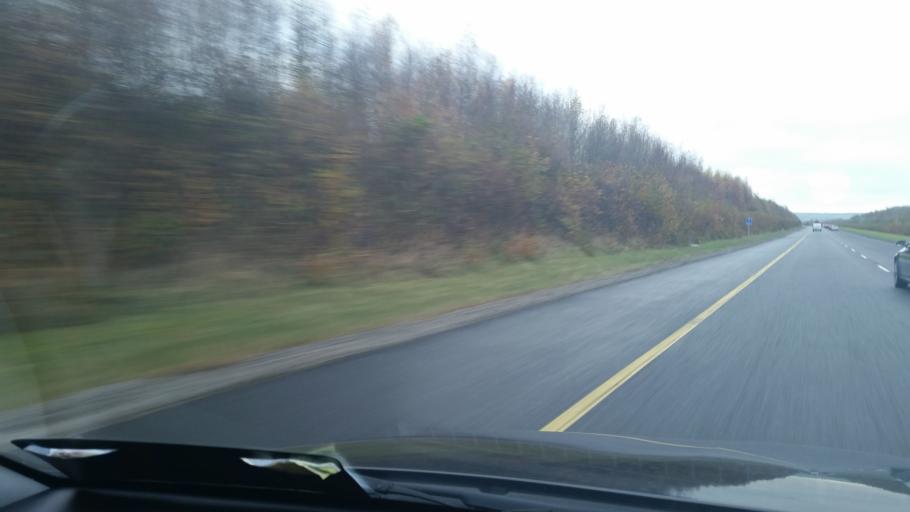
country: IE
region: Leinster
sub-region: Lu
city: Drogheda
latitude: 53.6851
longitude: -6.3643
